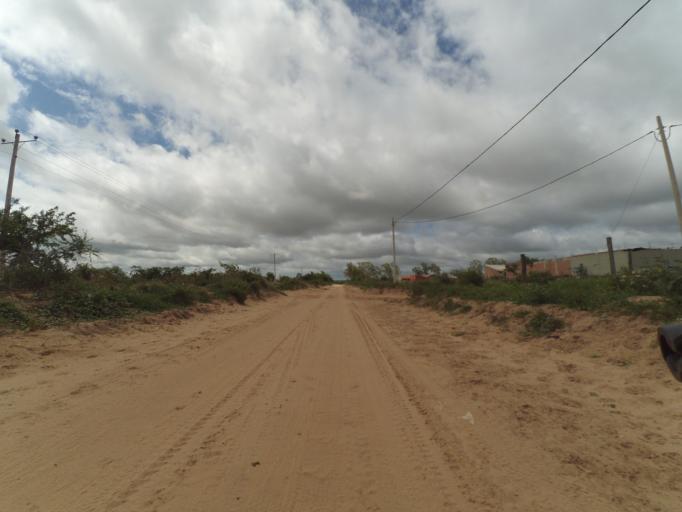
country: BO
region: Santa Cruz
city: Santa Cruz de la Sierra
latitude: -17.8826
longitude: -63.2370
